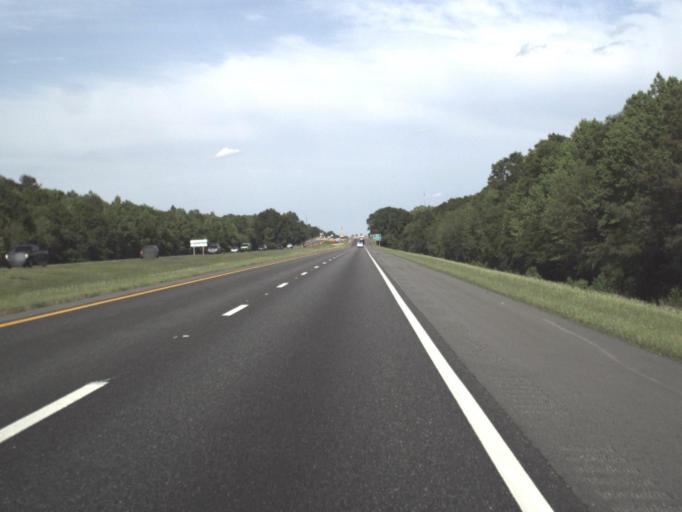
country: US
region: Florida
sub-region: Holmes County
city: Bonifay
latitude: 30.7540
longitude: -85.8400
